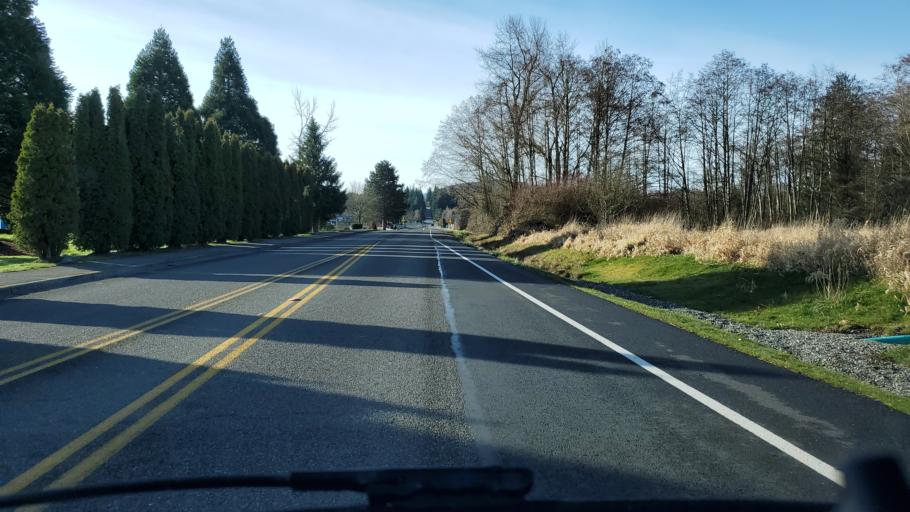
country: US
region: Washington
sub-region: Skagit County
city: Mount Vernon
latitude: 48.4345
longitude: -122.3026
